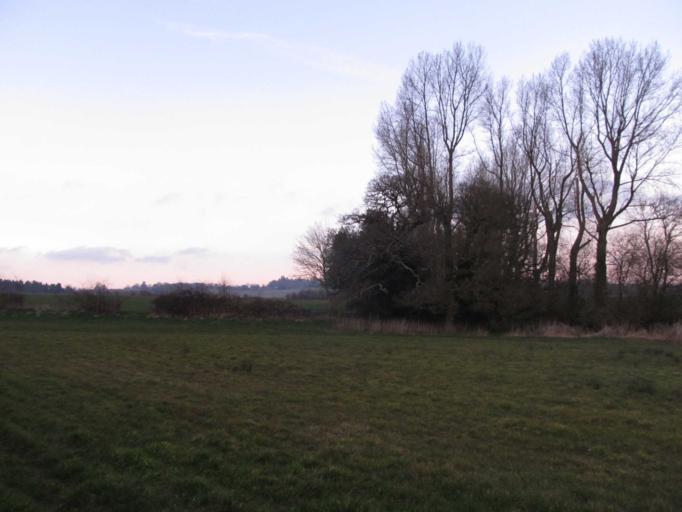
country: GB
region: England
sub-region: West Sussex
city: Petworth
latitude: 50.9818
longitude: -0.6635
